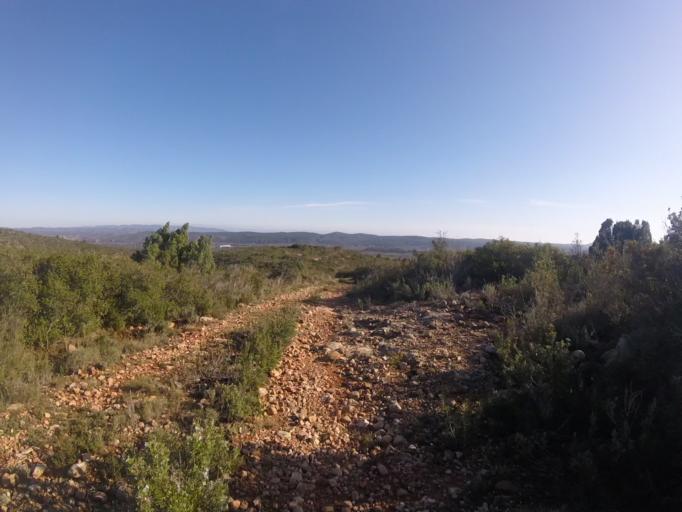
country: ES
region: Valencia
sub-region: Provincia de Castello
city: Sarratella
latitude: 40.2893
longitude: 0.0556
